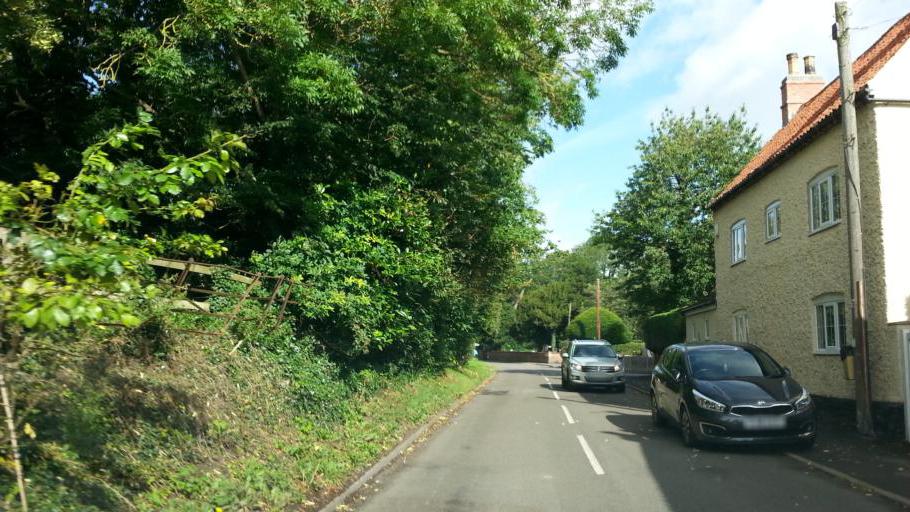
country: GB
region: England
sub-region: Nottinghamshire
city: Farndon
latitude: 53.0226
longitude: -0.8689
